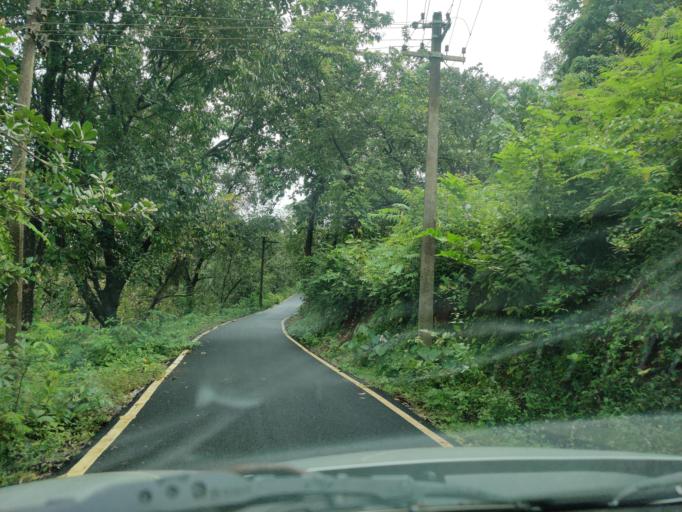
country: IN
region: Goa
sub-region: North Goa
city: Valpoy
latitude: 15.5292
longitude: 74.1423
